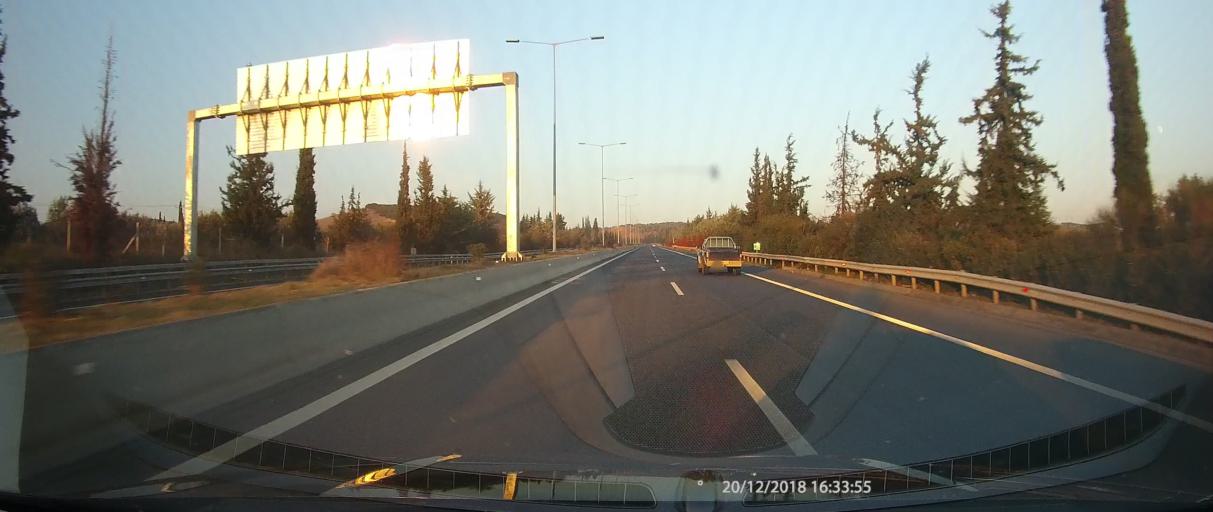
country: GR
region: Thessaly
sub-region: Nomos Magnisias
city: Nea Anchialos
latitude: 39.2732
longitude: 22.7396
